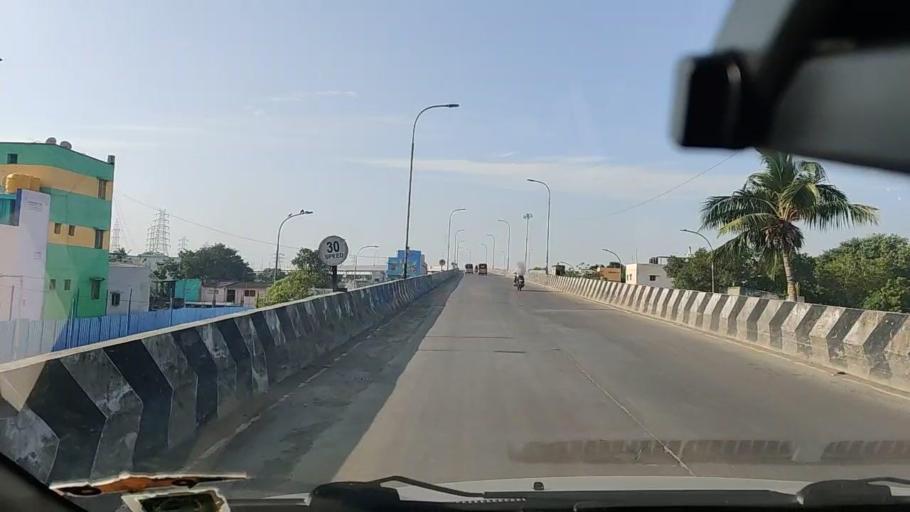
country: IN
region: Tamil Nadu
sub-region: Chennai
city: George Town
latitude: 13.1133
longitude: 80.2657
